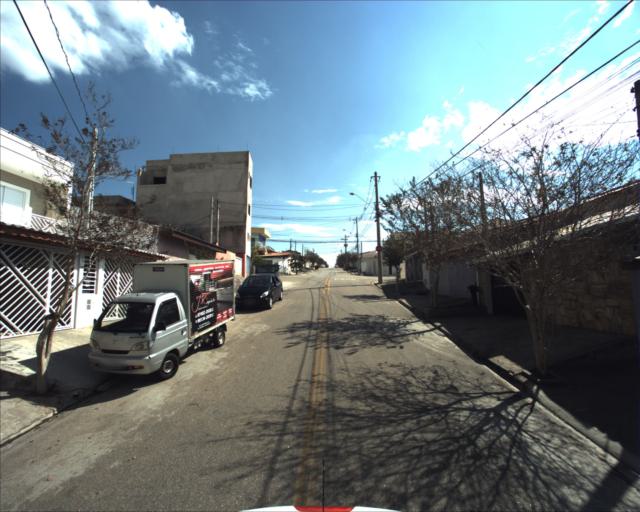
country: BR
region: Sao Paulo
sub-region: Sorocaba
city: Sorocaba
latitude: -23.4772
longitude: -47.5093
